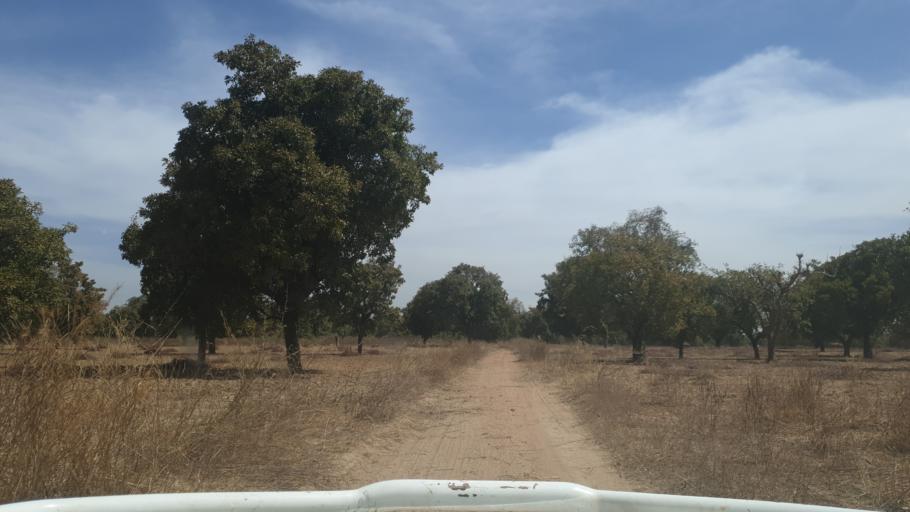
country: ML
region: Sikasso
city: Yorosso
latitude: 12.2884
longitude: -4.6725
